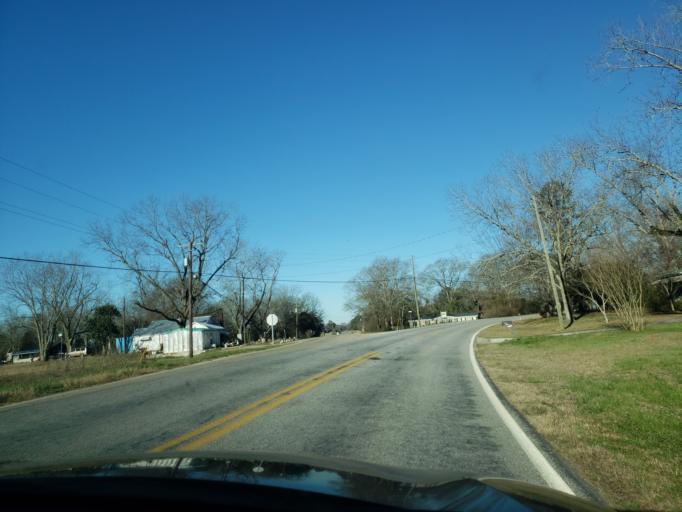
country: US
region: Alabama
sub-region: Elmore County
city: Tallassee
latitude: 32.5812
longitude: -85.7880
